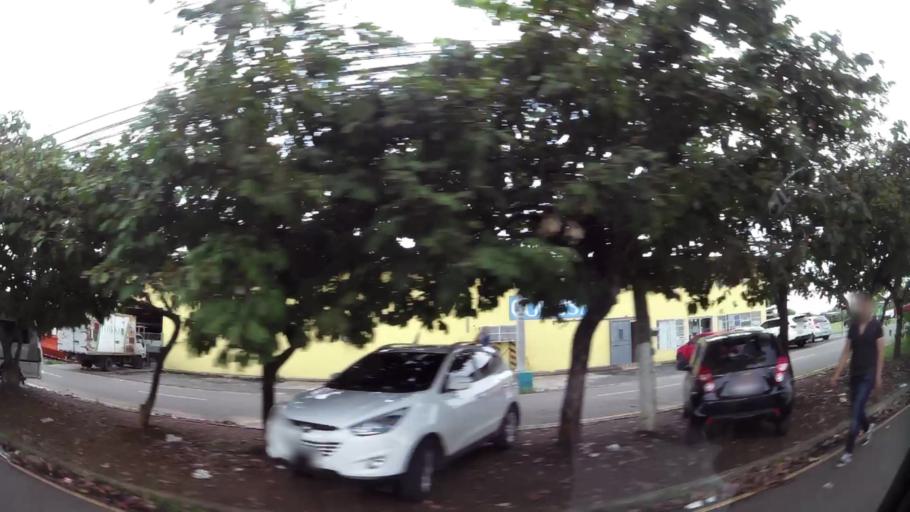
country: PA
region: Panama
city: Cabra Numero Uno
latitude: 9.0950
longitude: -79.3478
